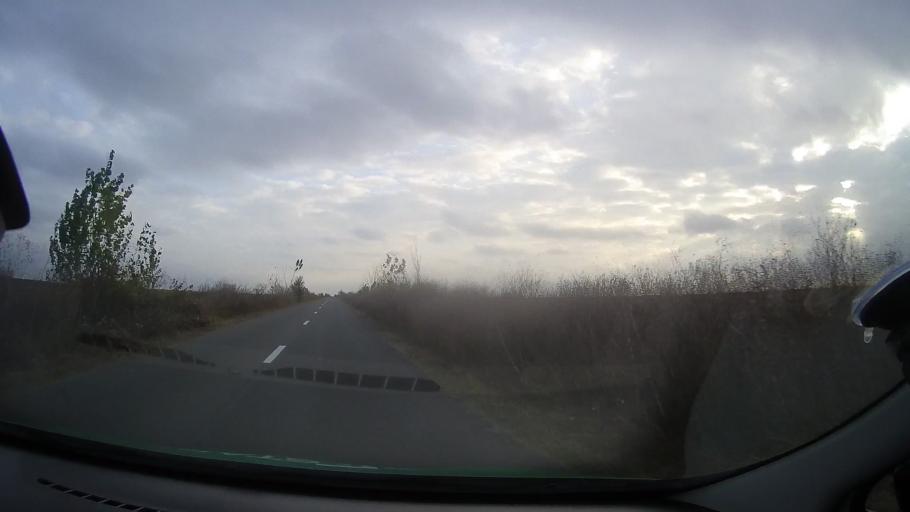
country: RO
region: Constanta
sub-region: Comuna Pestera
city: Pestera
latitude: 44.1422
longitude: 28.1166
